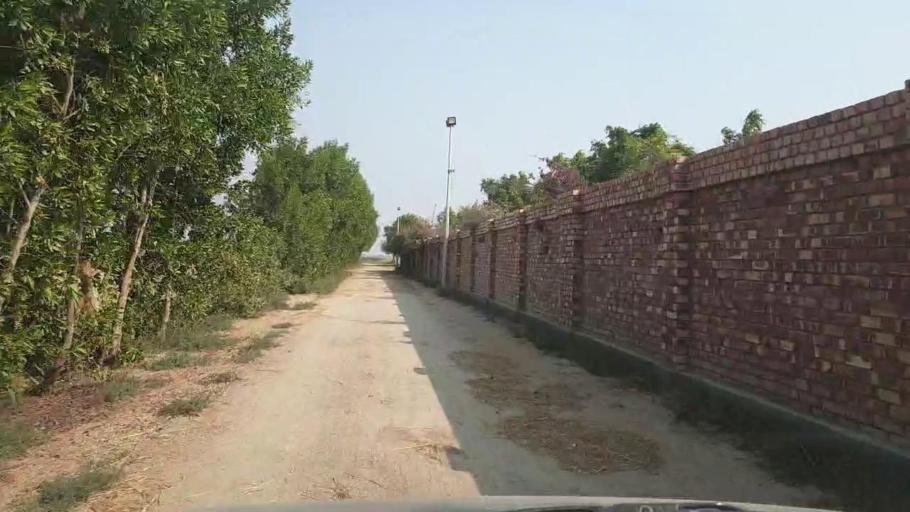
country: PK
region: Sindh
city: Bulri
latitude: 25.0351
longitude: 68.3832
